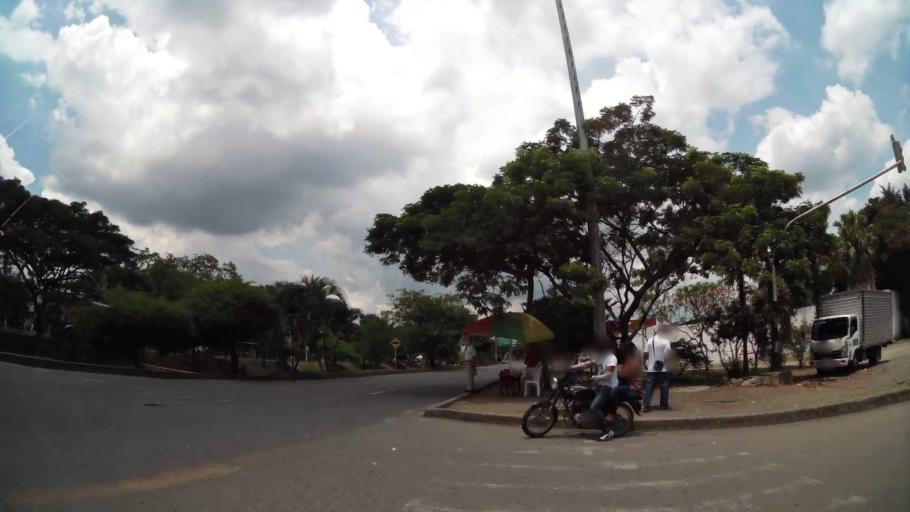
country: CO
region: Valle del Cauca
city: Cali
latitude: 3.4645
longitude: -76.4797
